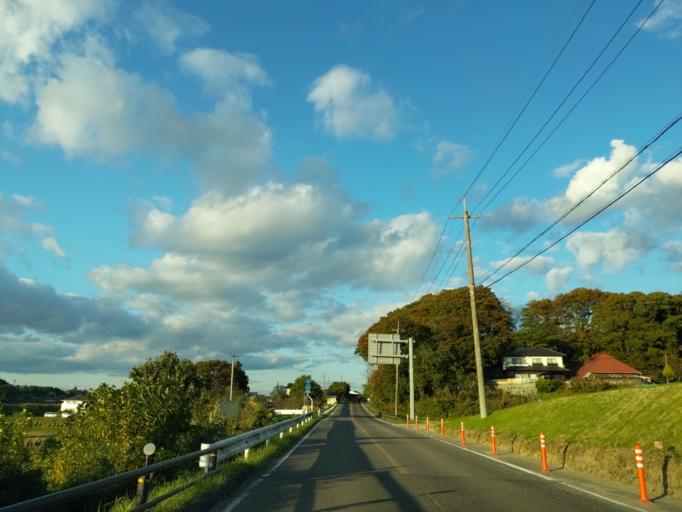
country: JP
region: Fukushima
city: Koriyama
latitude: 37.4294
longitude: 140.4193
